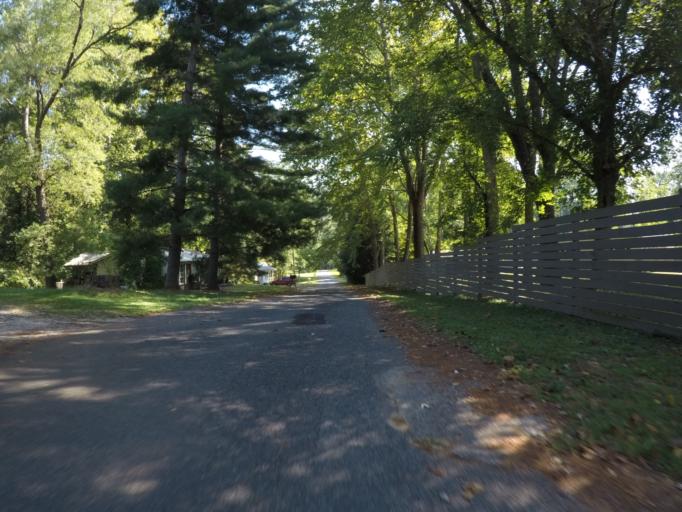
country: US
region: West Virginia
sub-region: Cabell County
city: Barboursville
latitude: 38.3750
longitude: -82.2803
